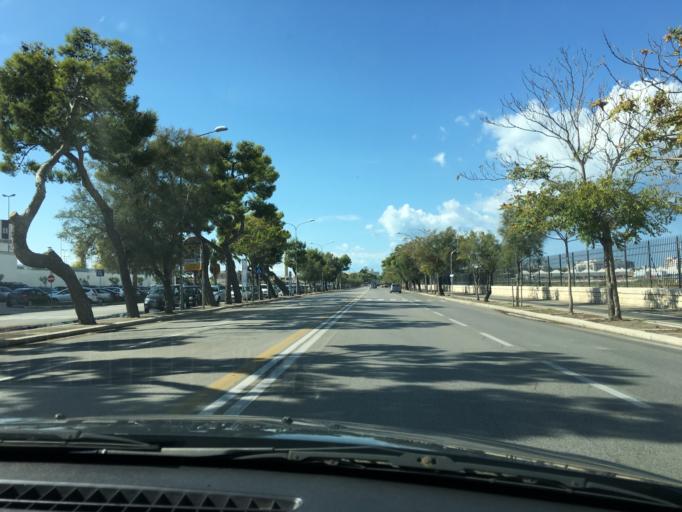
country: IT
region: Apulia
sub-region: Provincia di Bari
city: Bari
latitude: 41.1298
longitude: 16.8507
